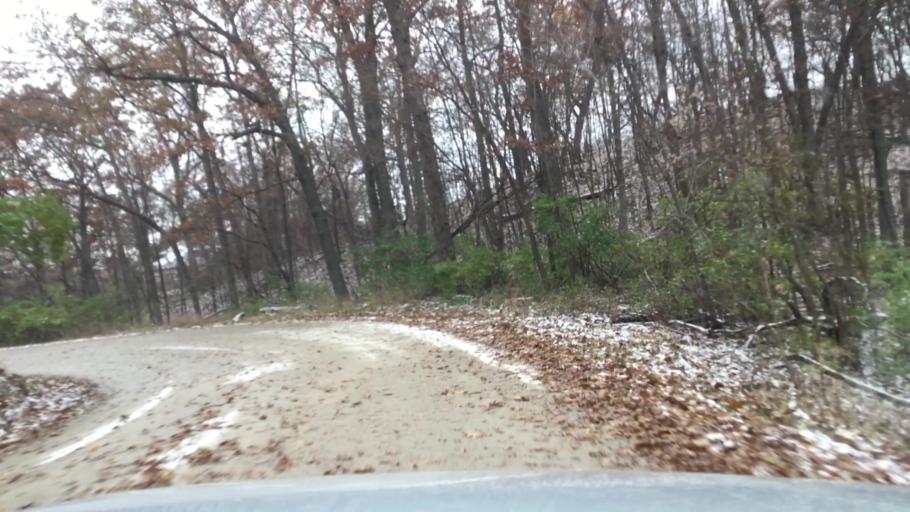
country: US
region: Michigan
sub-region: Livingston County
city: Brighton
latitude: 42.5398
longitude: -83.7112
